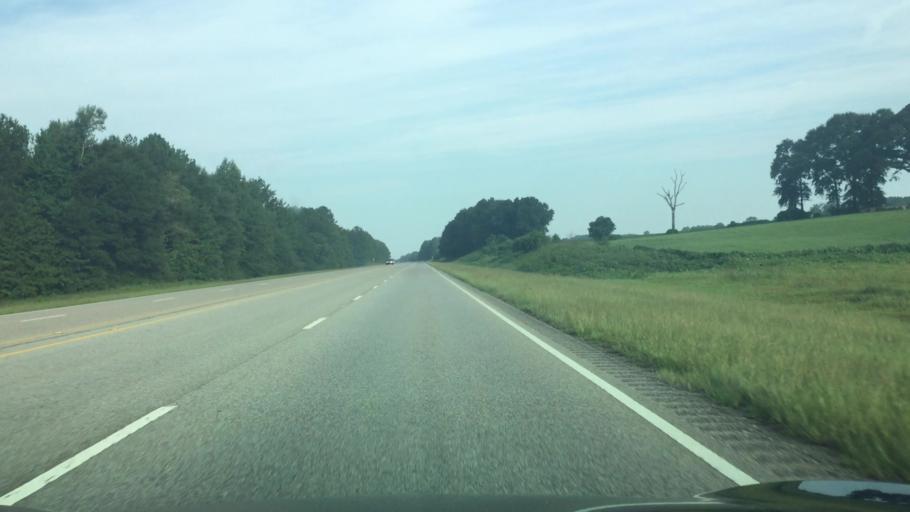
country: US
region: Alabama
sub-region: Covington County
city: Andalusia
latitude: 31.3994
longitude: -86.5811
